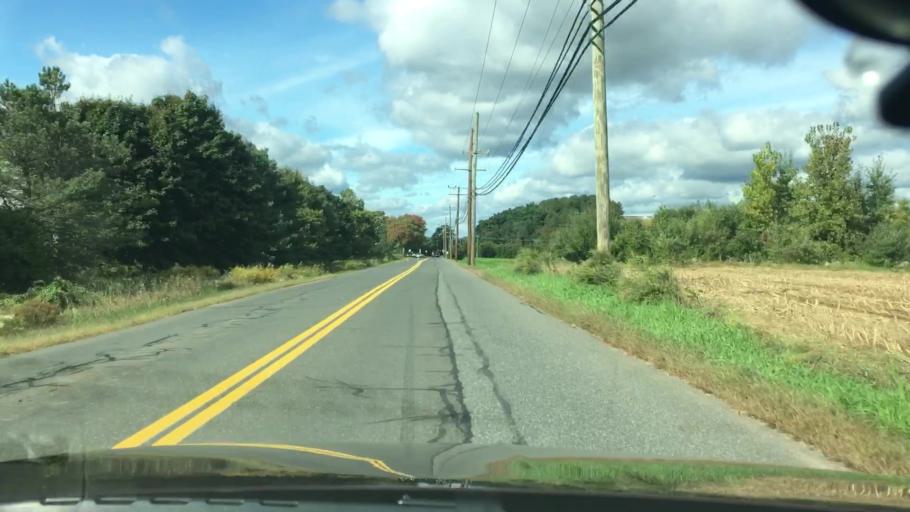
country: US
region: Connecticut
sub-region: Hartford County
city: Hazardville
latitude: 42.0113
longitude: -72.5130
